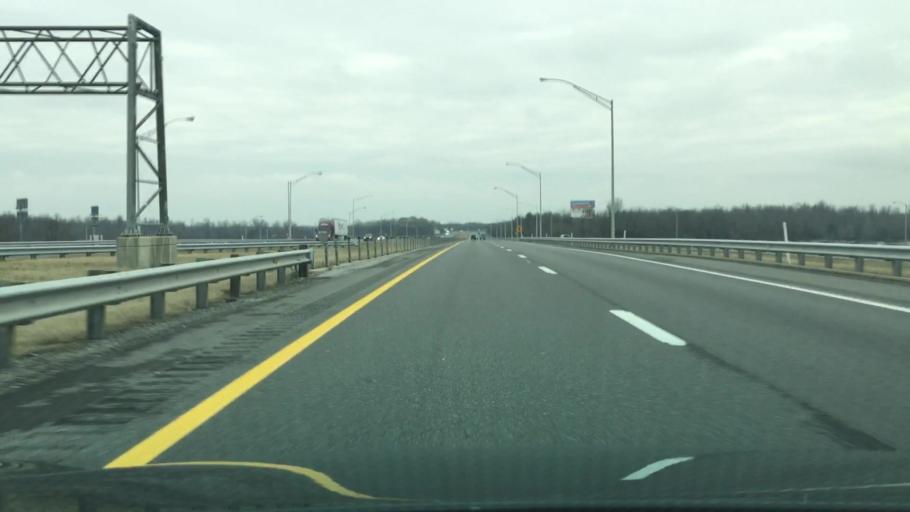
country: US
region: Illinois
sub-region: Massac County
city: Metropolis
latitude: 37.0981
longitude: -88.6882
